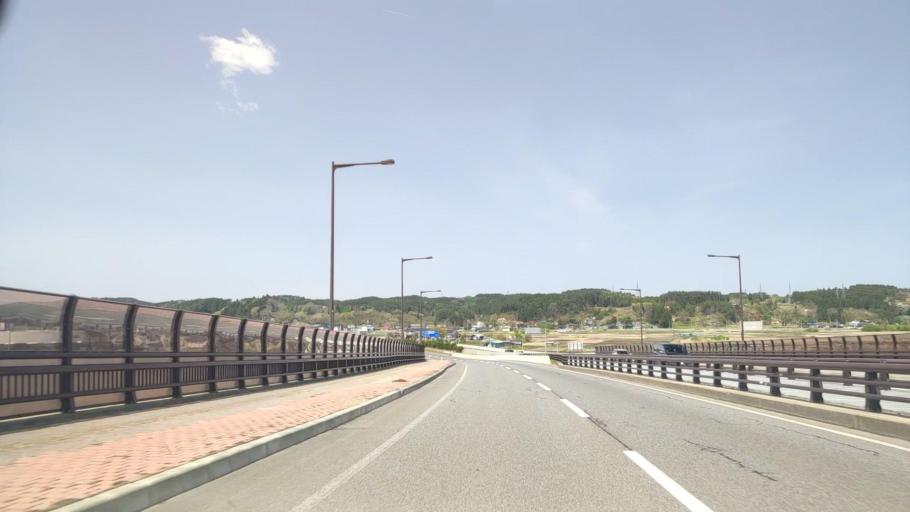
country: JP
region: Aomori
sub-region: Hachinohe Shi
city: Uchimaru
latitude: 40.5158
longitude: 141.4358
